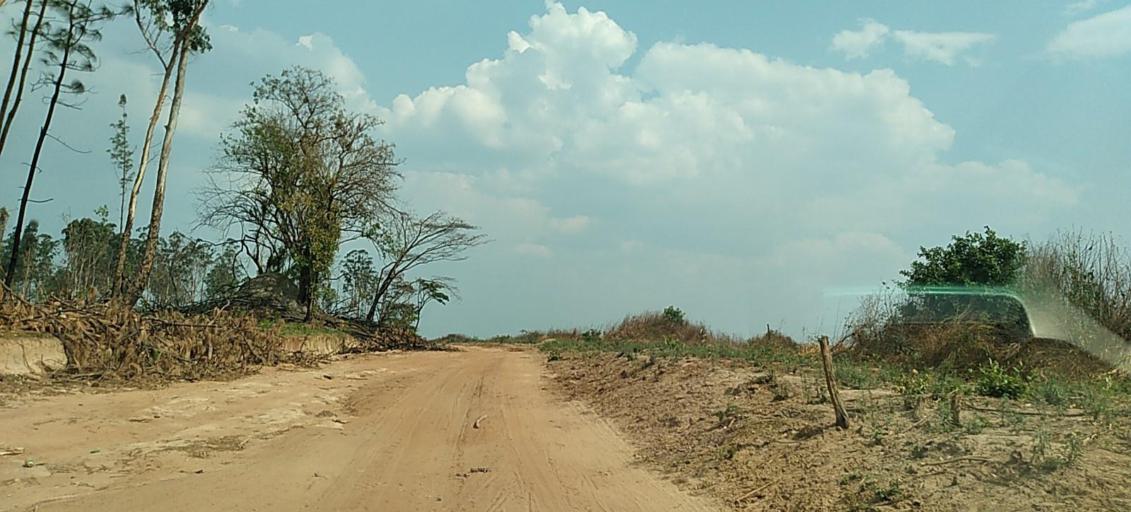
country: ZM
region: Copperbelt
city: Chingola
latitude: -12.7551
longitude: 27.7900
